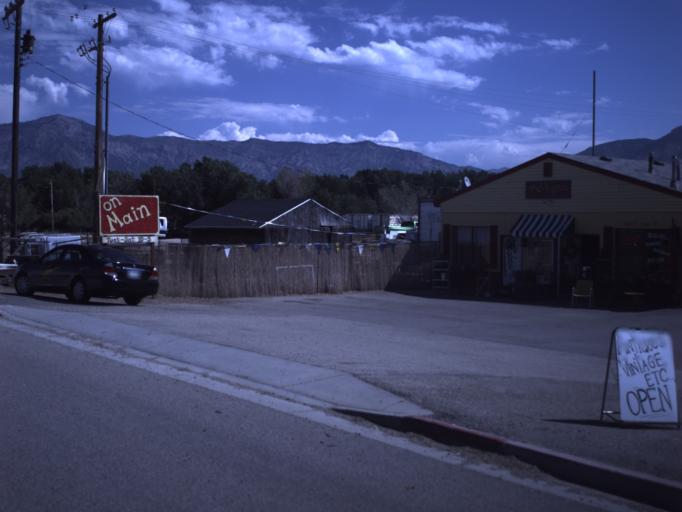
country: US
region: Utah
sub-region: Weber County
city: Marriott-Slaterville
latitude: 41.2366
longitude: -112.0254
